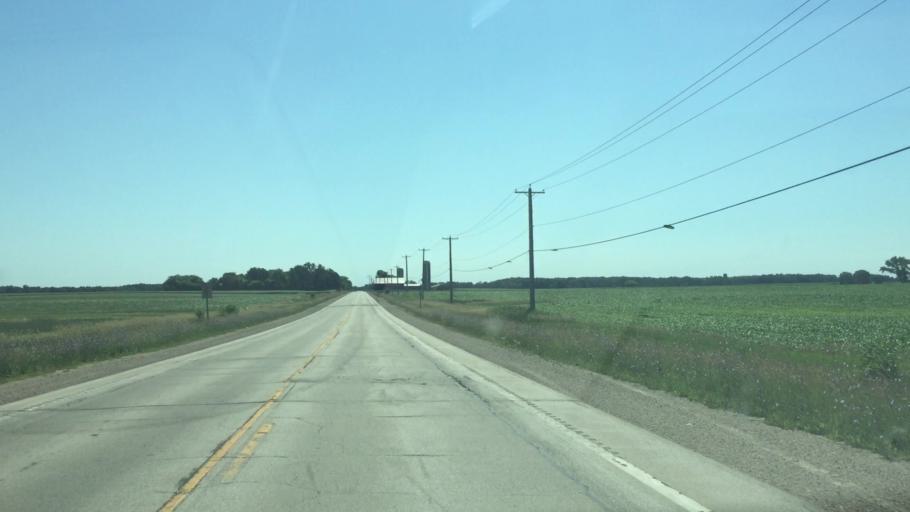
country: US
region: Wisconsin
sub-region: Calumet County
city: Hilbert
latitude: 44.1403
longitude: -88.2012
